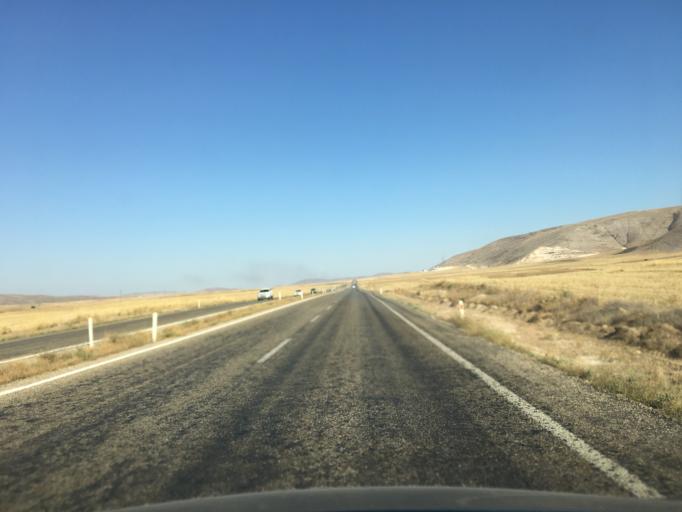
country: TR
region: Kirsehir
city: Akpinar
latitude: 39.3420
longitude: 33.9691
